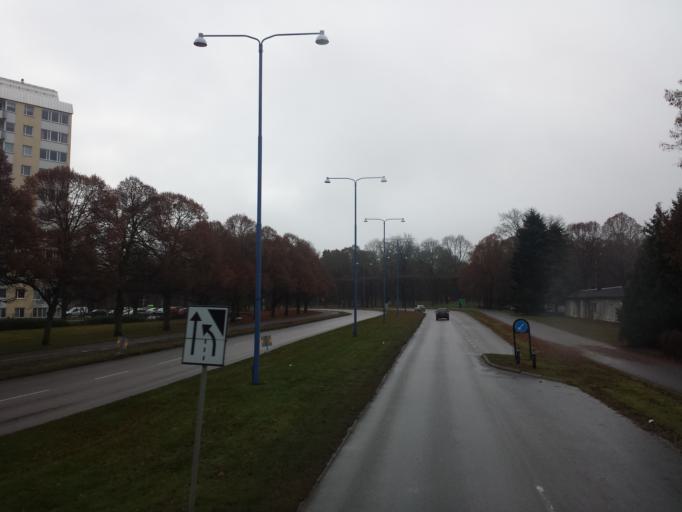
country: SE
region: OEstergoetland
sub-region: Norrkopings Kommun
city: Norrkoping
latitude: 58.5940
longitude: 16.1610
